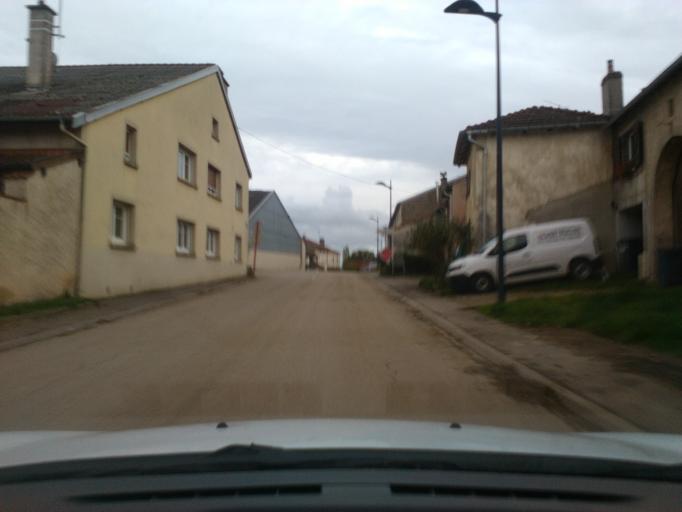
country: FR
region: Lorraine
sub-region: Departement des Vosges
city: Mirecourt
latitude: 48.3356
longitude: 6.0968
